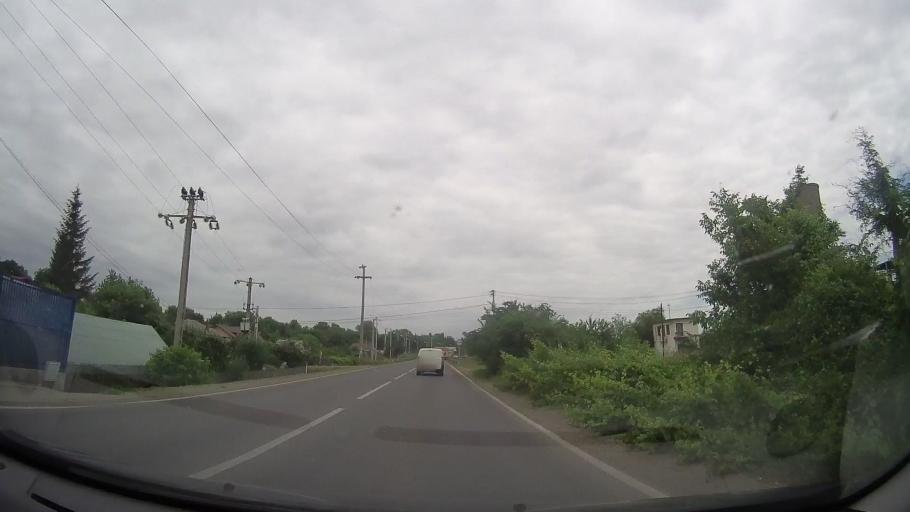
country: RO
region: Prahova
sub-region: Comuna Blejoiu
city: Blejoi
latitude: 44.9910
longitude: 26.0142
